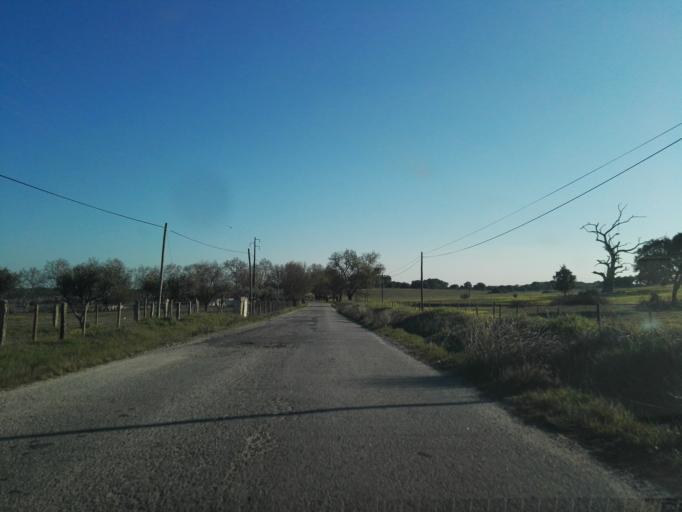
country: PT
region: Evora
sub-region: Evora
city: Evora
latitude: 38.5326
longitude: -7.9501
